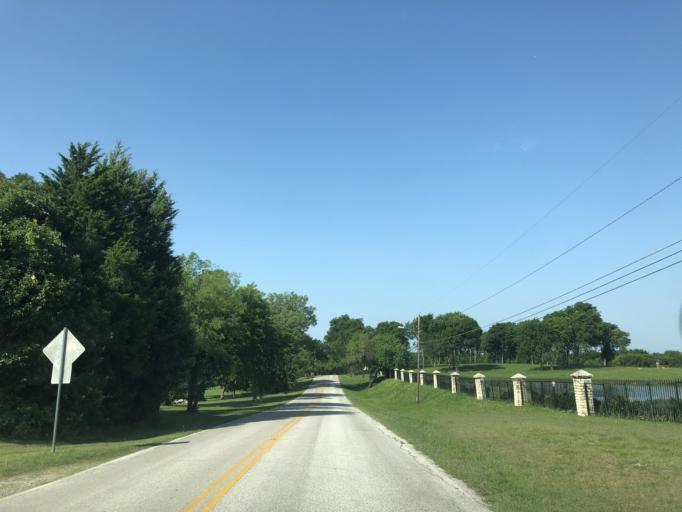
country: US
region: Texas
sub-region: Dallas County
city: Sunnyvale
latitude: 32.8329
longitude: -96.5615
